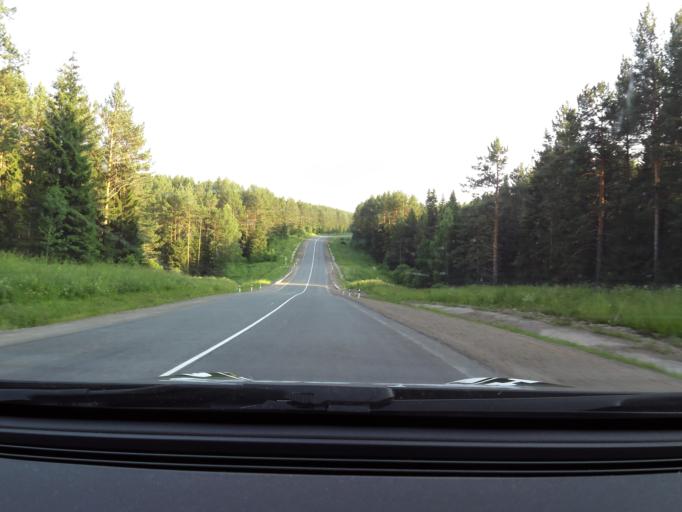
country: RU
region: Sverdlovsk
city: Nizhniye Sergi
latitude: 56.6313
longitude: 59.2413
